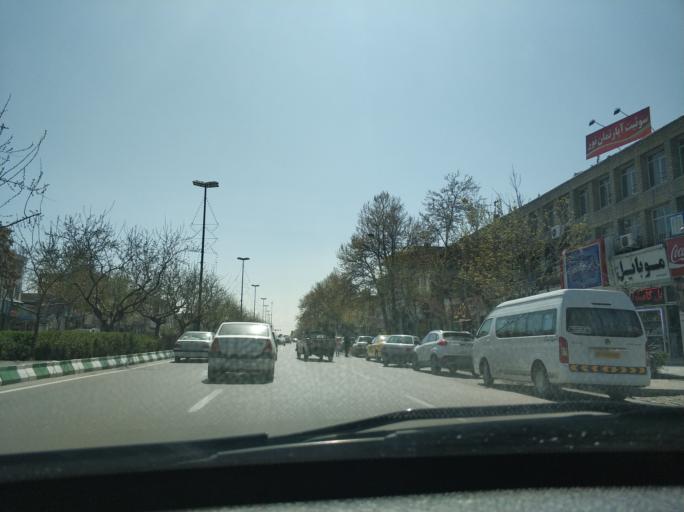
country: IR
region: Razavi Khorasan
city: Mashhad
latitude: 36.2600
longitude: 59.6065
